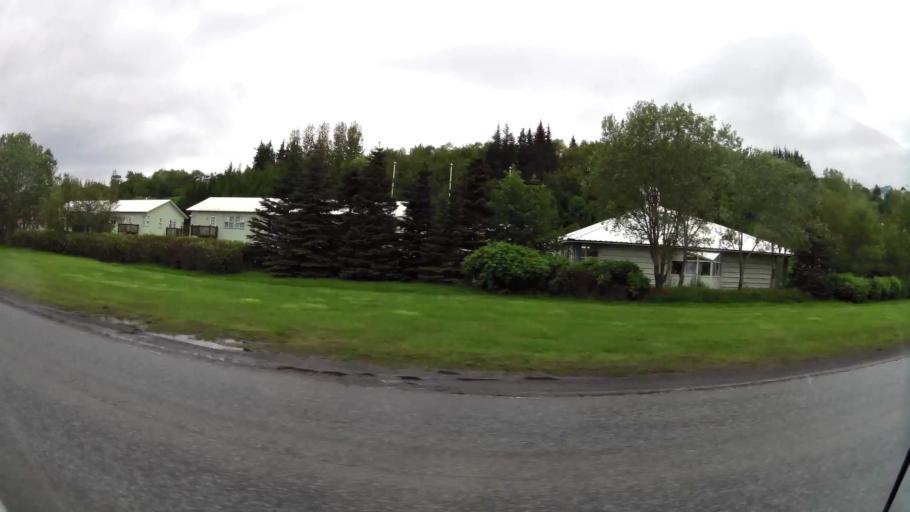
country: IS
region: Northeast
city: Akureyri
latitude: 65.6748
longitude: -18.0871
